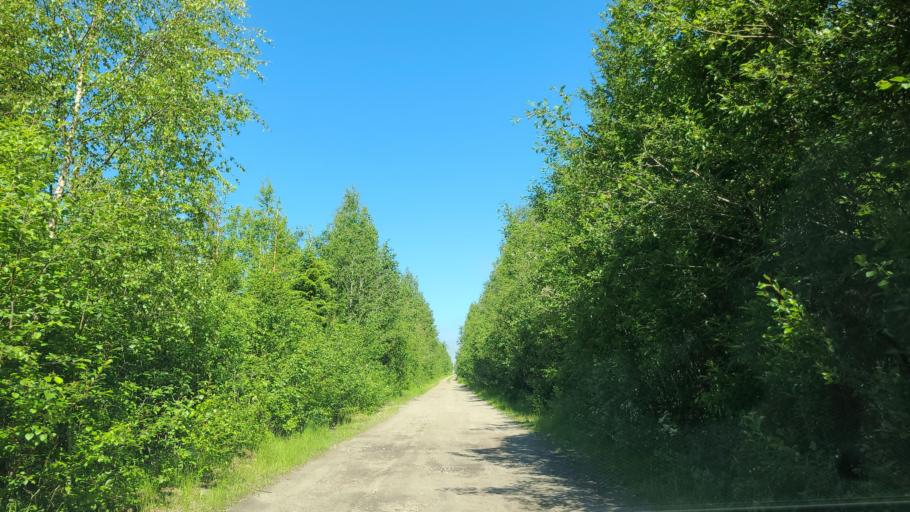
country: SE
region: Vaesternorrland
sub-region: OErnskoeldsviks Kommun
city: Husum
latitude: 63.4228
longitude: 19.2243
